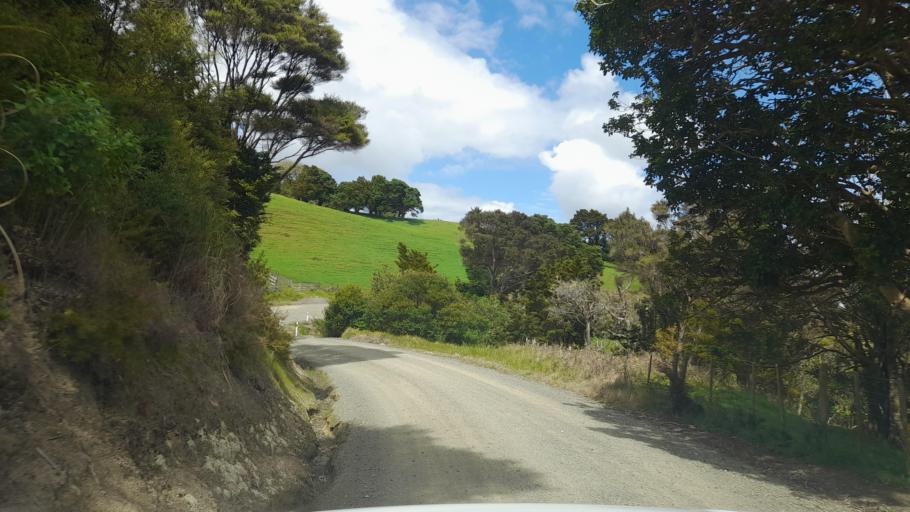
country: NZ
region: Auckland
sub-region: Auckland
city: Wellsford
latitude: -36.2069
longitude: 174.3356
